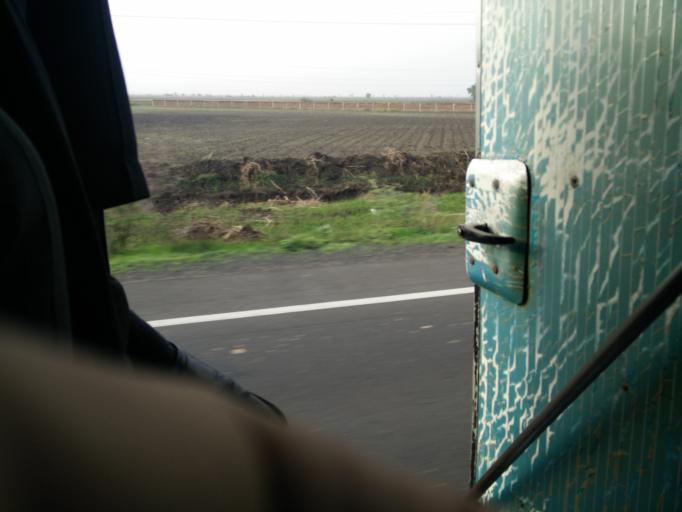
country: IN
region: Gujarat
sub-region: Ahmadabad
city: Dholka
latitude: 22.7319
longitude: 72.2799
